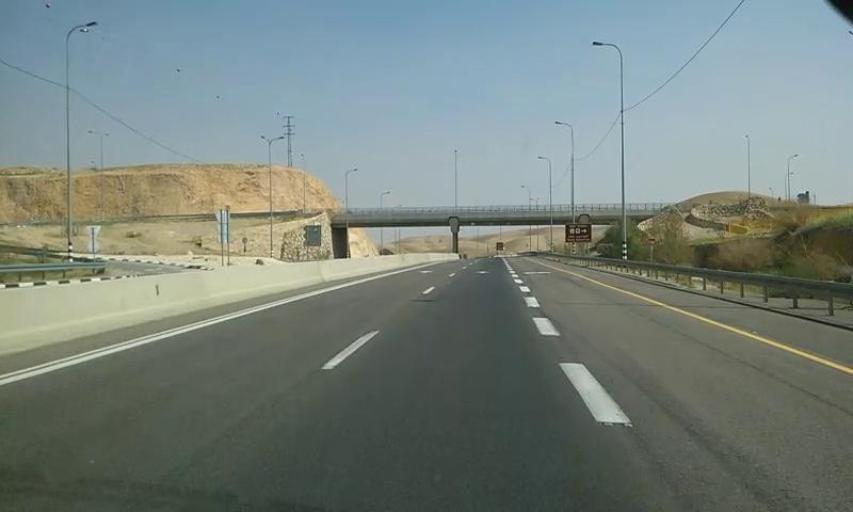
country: PS
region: West Bank
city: Hizma
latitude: 31.8169
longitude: 35.3624
